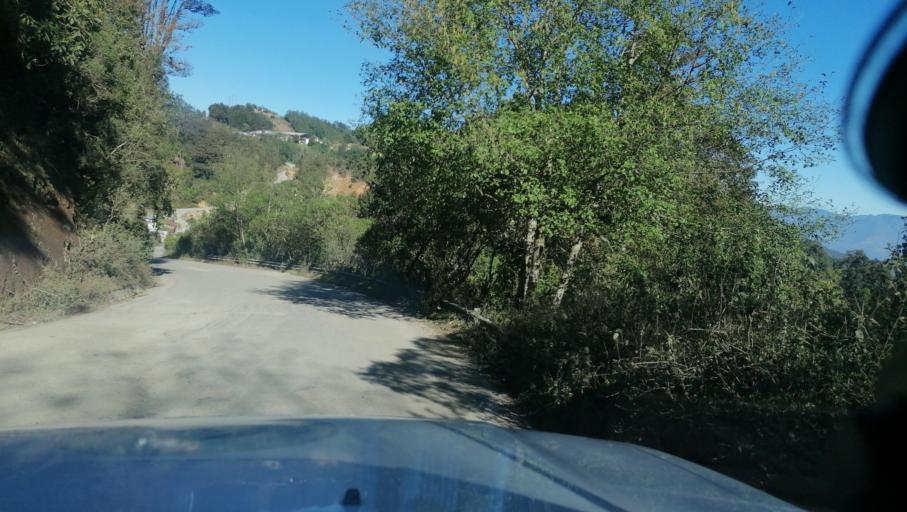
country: MX
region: Chiapas
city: Motozintla de Mendoza
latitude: 15.2655
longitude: -92.2199
